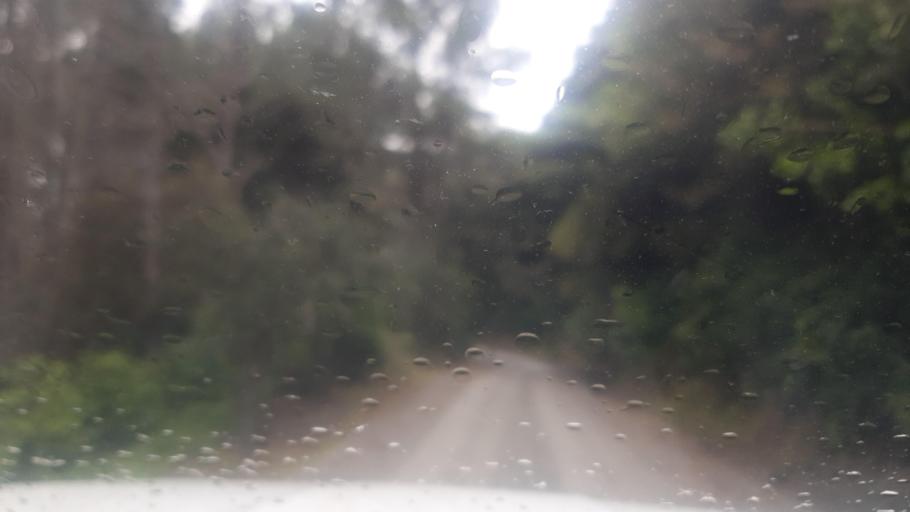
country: NZ
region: Northland
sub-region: Far North District
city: Taipa
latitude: -35.0857
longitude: 173.3907
